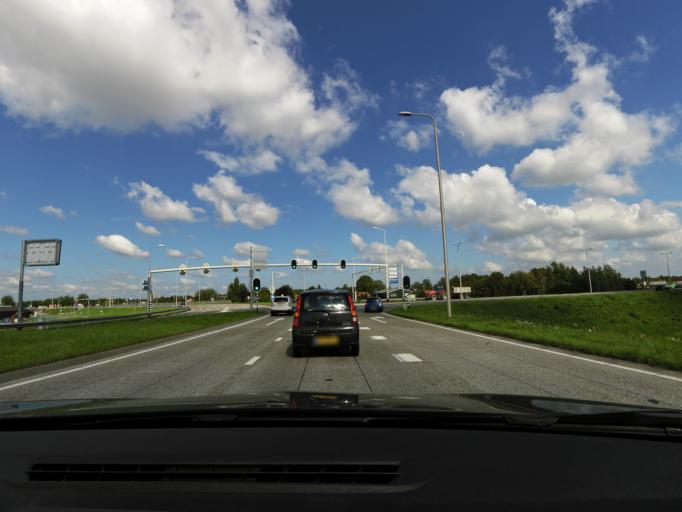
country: NL
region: South Holland
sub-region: Gemeente Alphen aan den Rijn
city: Alphen aan den Rijn
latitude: 52.1147
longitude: 4.6769
